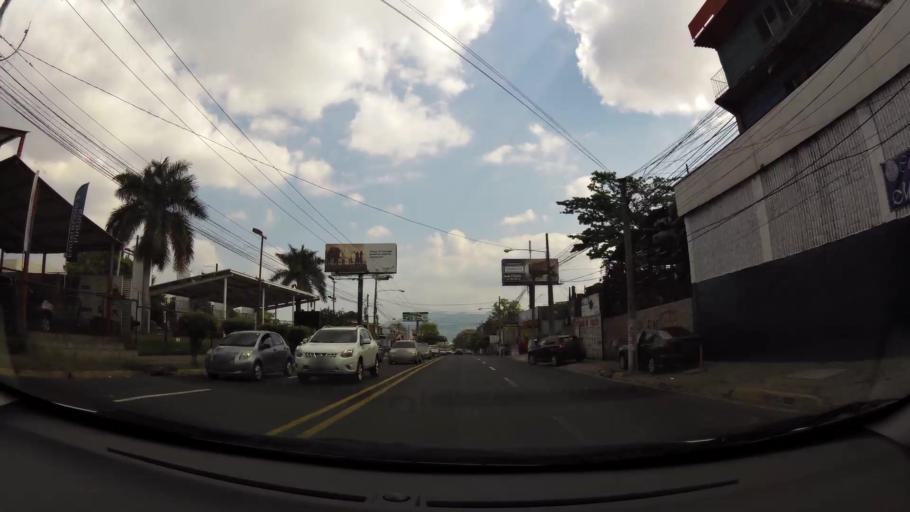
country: SV
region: San Salvador
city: Mejicanos
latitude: 13.7091
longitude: -89.2297
